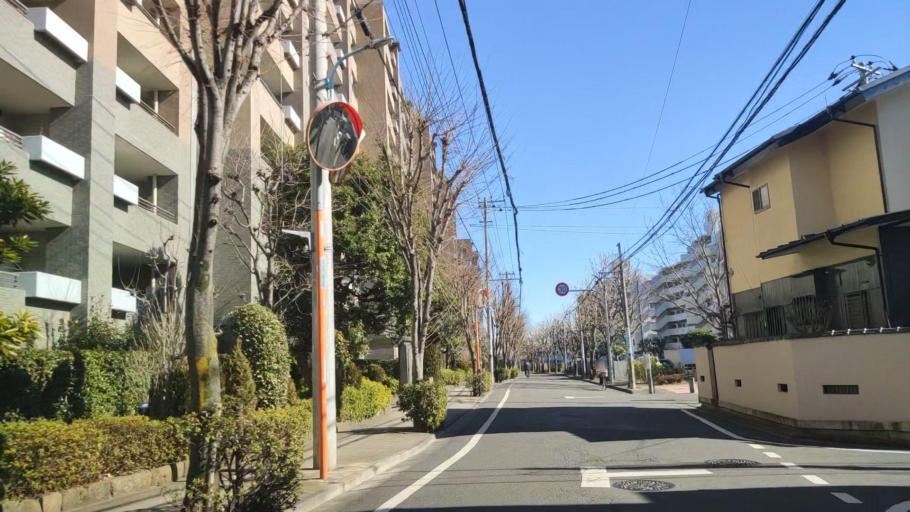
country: JP
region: Tokyo
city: Nishi-Tokyo-shi
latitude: 35.7228
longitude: 139.5521
